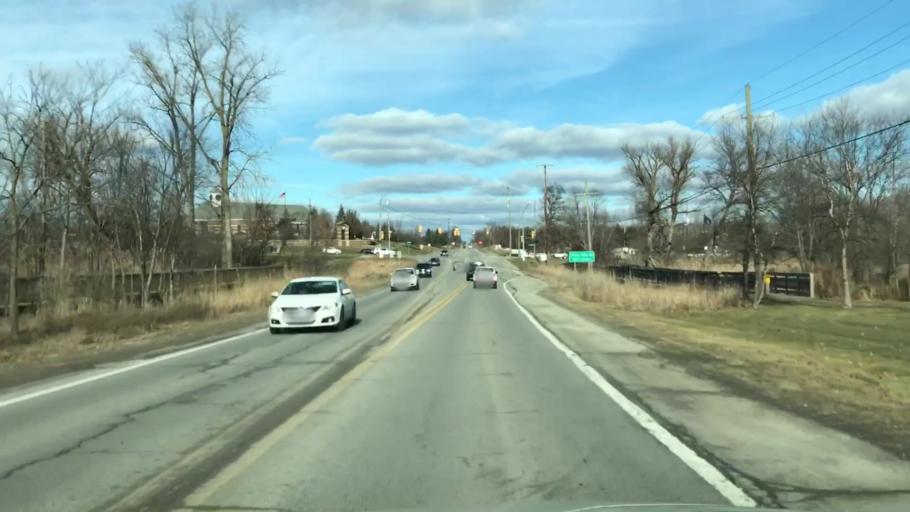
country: US
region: Michigan
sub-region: Oakland County
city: Auburn Hills
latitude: 42.7222
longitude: -83.1962
